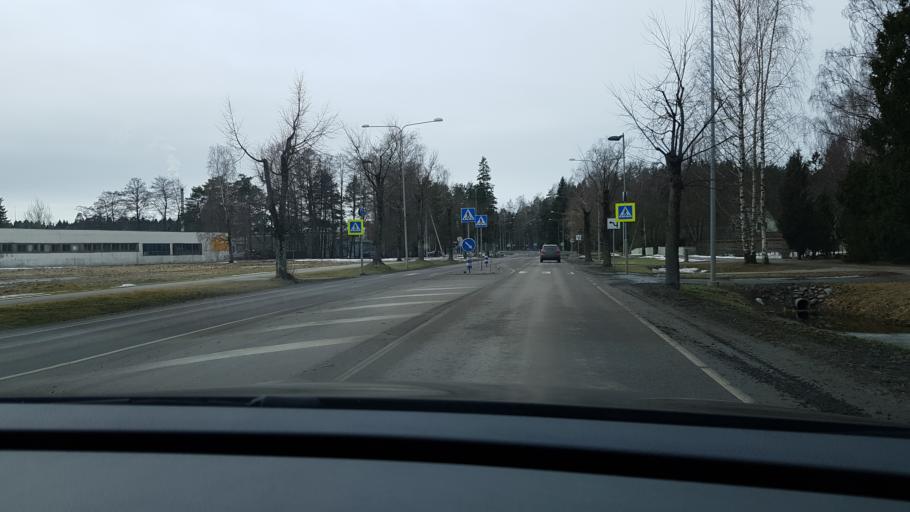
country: EE
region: Paernumaa
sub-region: Paikuse vald
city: Paikuse
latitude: 58.3741
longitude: 24.6173
